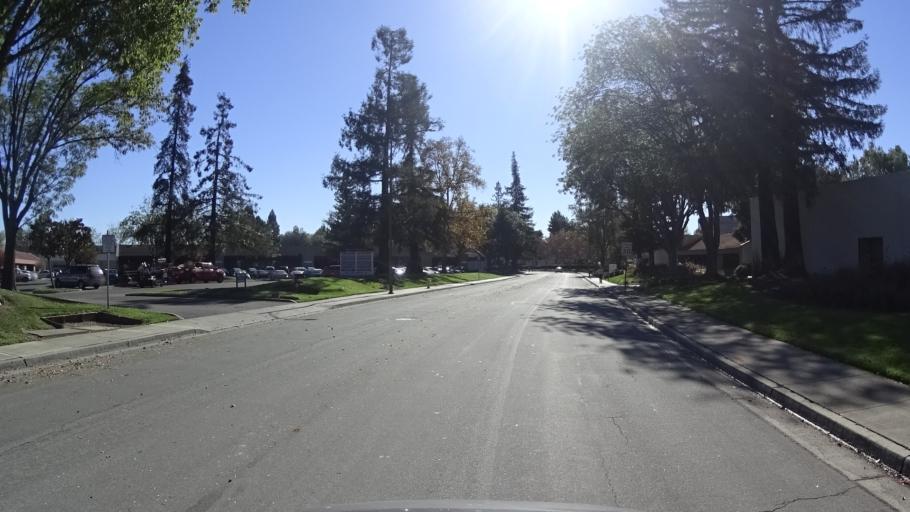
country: US
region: California
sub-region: Santa Clara County
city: Santa Clara
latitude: 37.3797
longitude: -121.9192
